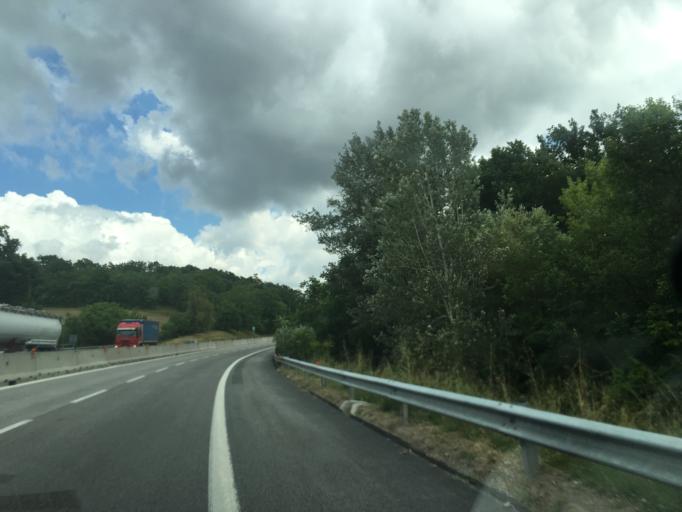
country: IT
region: Campania
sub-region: Provincia di Avellino
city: Passo di Mirabella-Pianopantano
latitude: 41.0697
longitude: 15.0029
